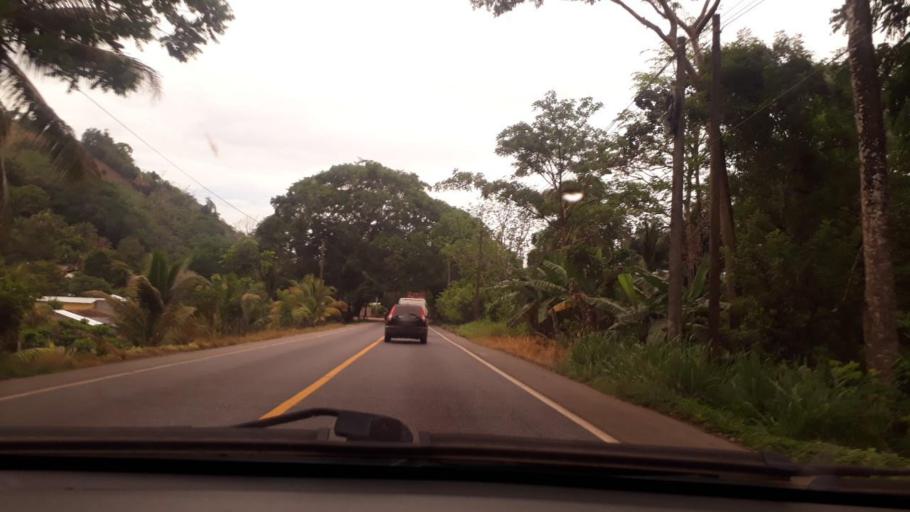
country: GT
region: Izabal
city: Morales
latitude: 15.5411
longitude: -88.7278
